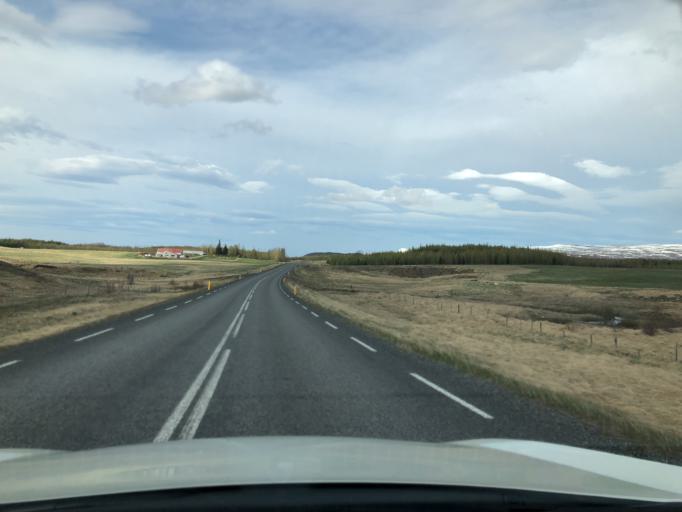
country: IS
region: East
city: Egilsstadir
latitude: 65.2144
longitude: -14.4762
